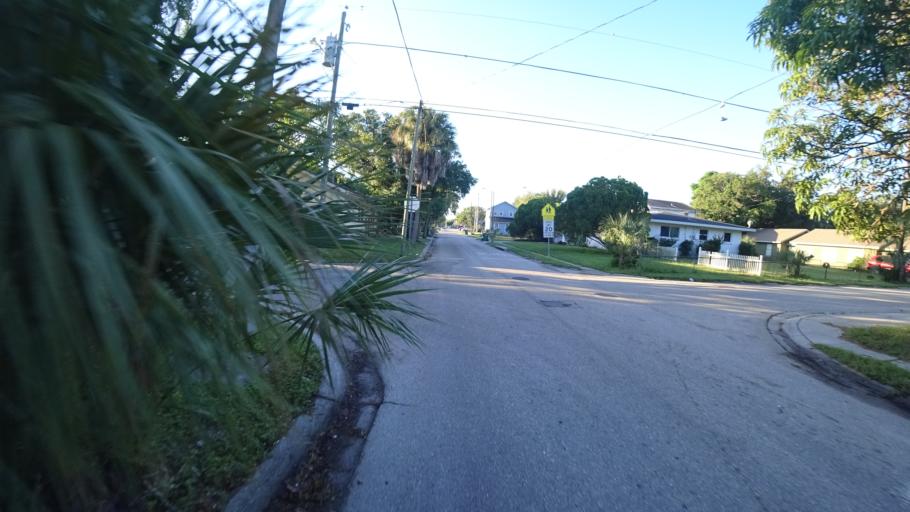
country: US
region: Florida
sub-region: Manatee County
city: Bradenton
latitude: 27.4891
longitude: -82.5681
